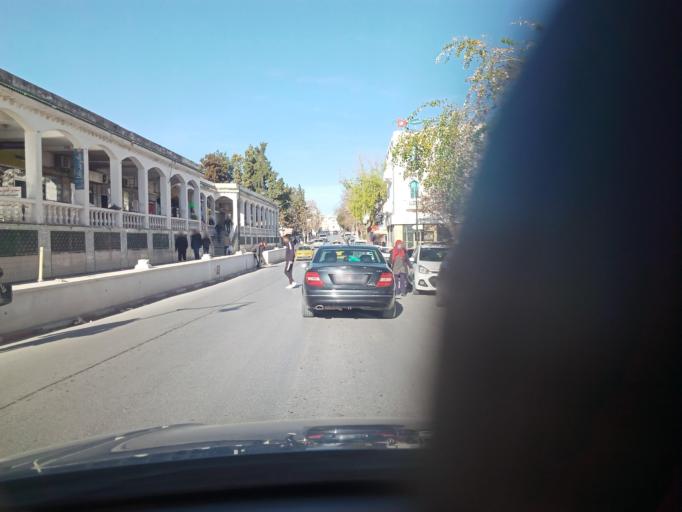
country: TN
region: Kef
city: El Kef
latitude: 36.1786
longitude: 8.7134
